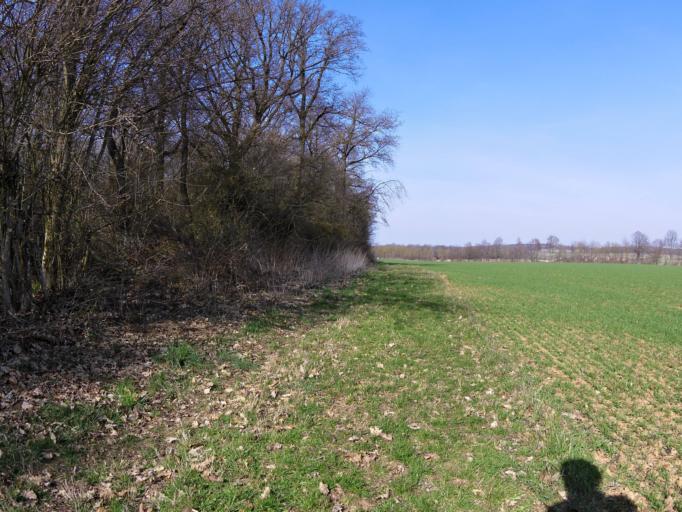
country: DE
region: Bavaria
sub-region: Regierungsbezirk Unterfranken
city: Rottendorf
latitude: 49.8092
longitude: 10.0409
